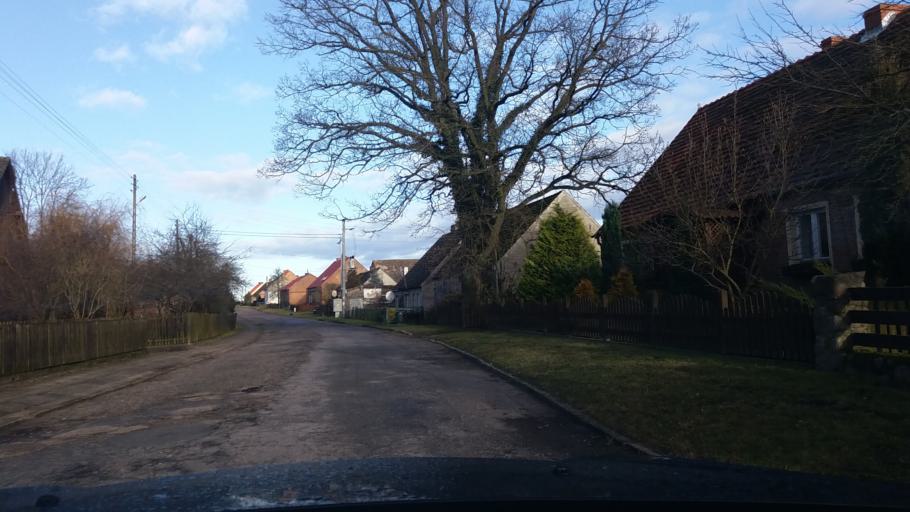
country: PL
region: West Pomeranian Voivodeship
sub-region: Powiat choszczenski
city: Drawno
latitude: 53.1771
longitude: 15.8041
